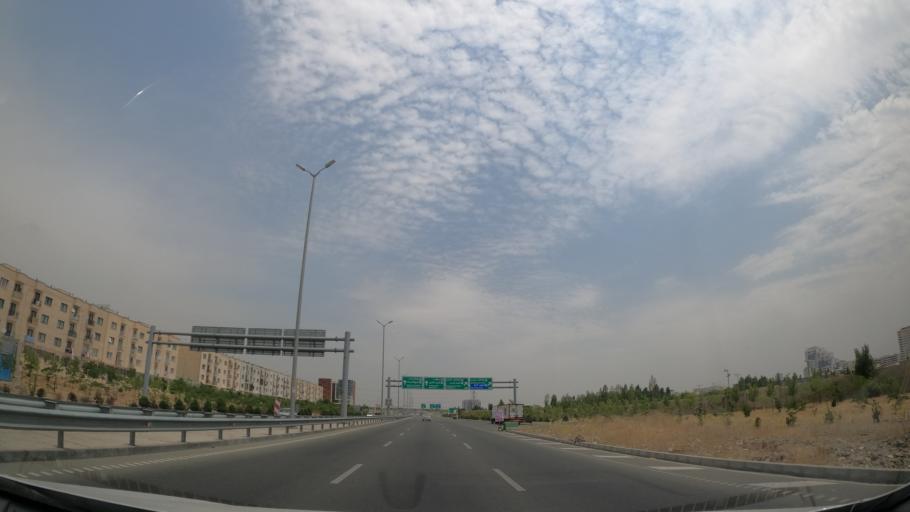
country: IR
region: Tehran
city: Shahr-e Qods
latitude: 35.7408
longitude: 51.2464
